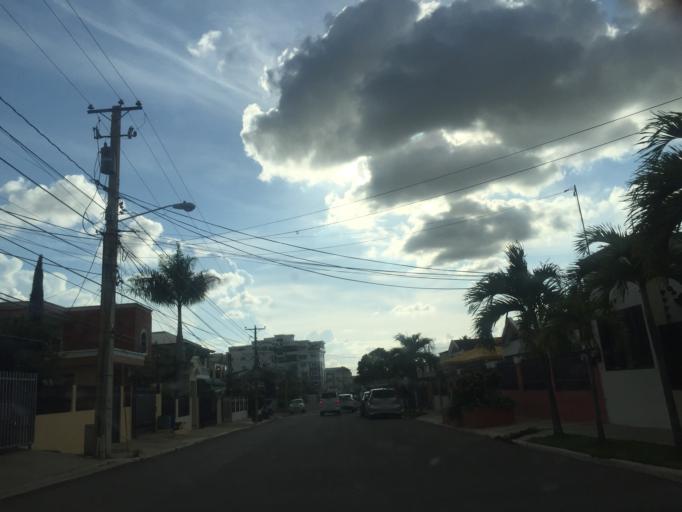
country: DO
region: Santiago
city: Santiago de los Caballeros
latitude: 19.4348
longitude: -70.6650
